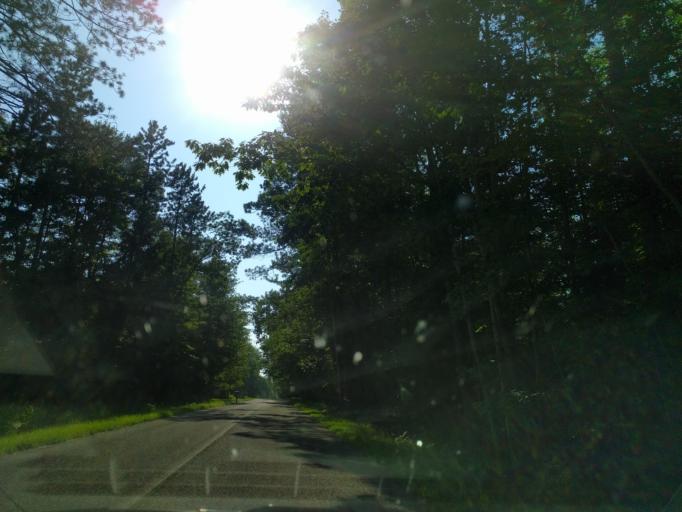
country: US
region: Michigan
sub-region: Delta County
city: Gladstone
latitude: 45.8913
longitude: -87.0522
